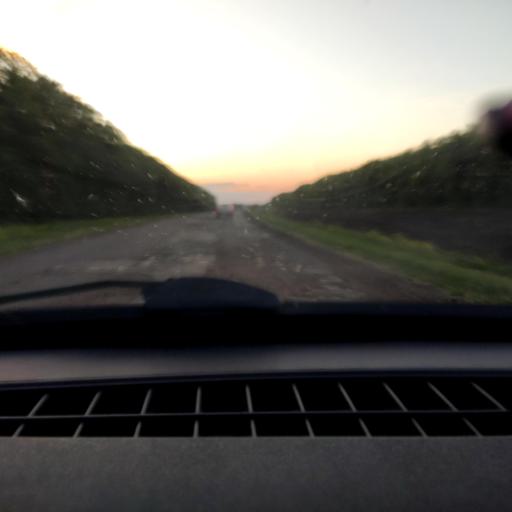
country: RU
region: Bashkortostan
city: Karmaskaly
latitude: 54.3920
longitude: 56.1727
